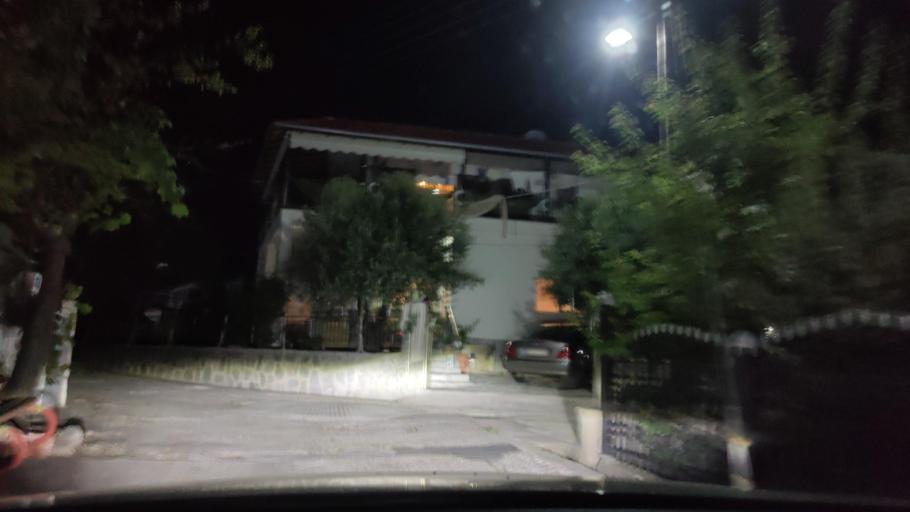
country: GR
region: Central Macedonia
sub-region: Nomos Serron
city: Neo Petritsi
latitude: 41.2769
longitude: 23.2911
